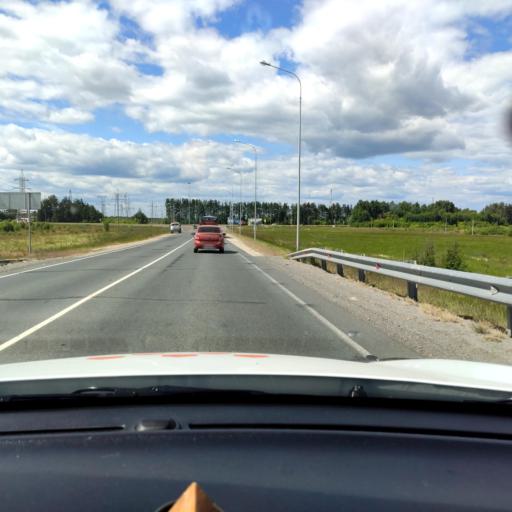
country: RU
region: Mariy-El
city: Volzhsk
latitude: 55.9105
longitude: 48.3706
